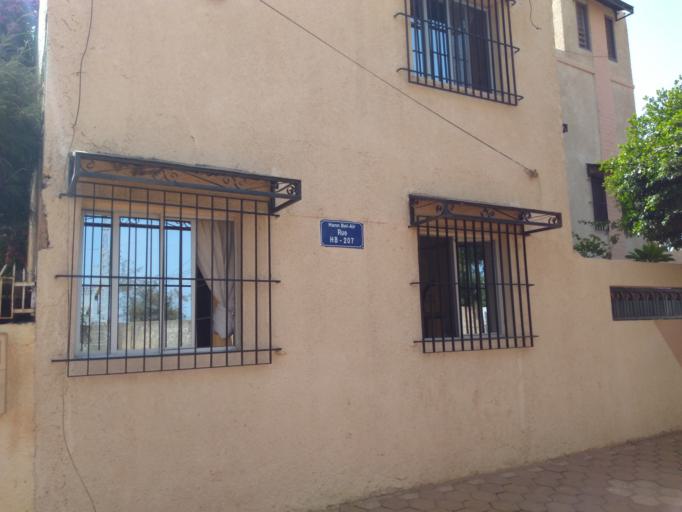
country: SN
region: Dakar
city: Grand Dakar
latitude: 14.7313
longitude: -17.4371
